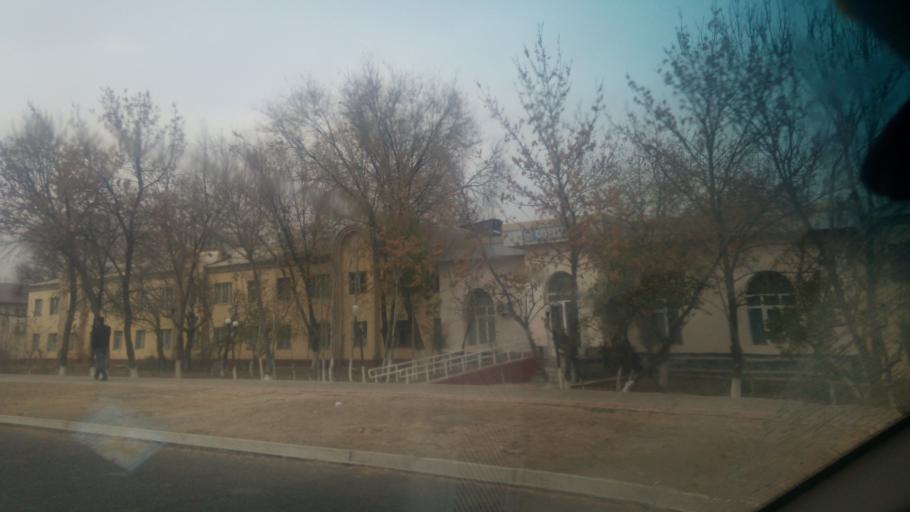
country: UZ
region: Sirdaryo
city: Guliston
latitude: 40.5091
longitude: 68.7731
